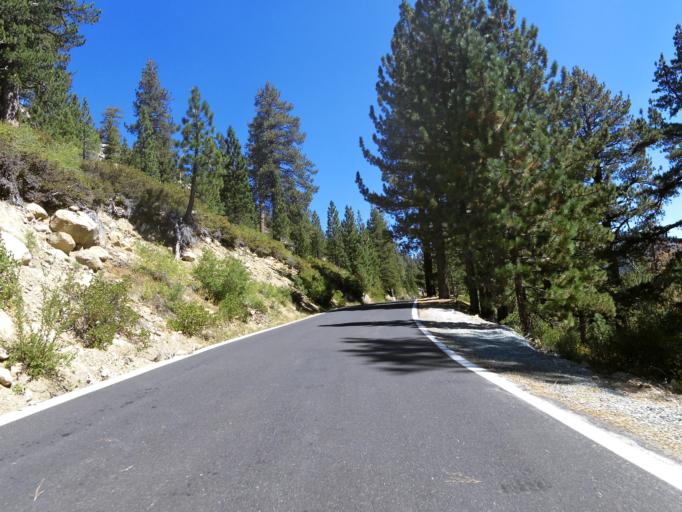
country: US
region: Nevada
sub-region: Douglas County
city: Gardnerville Ranchos
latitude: 38.5448
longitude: -119.8740
